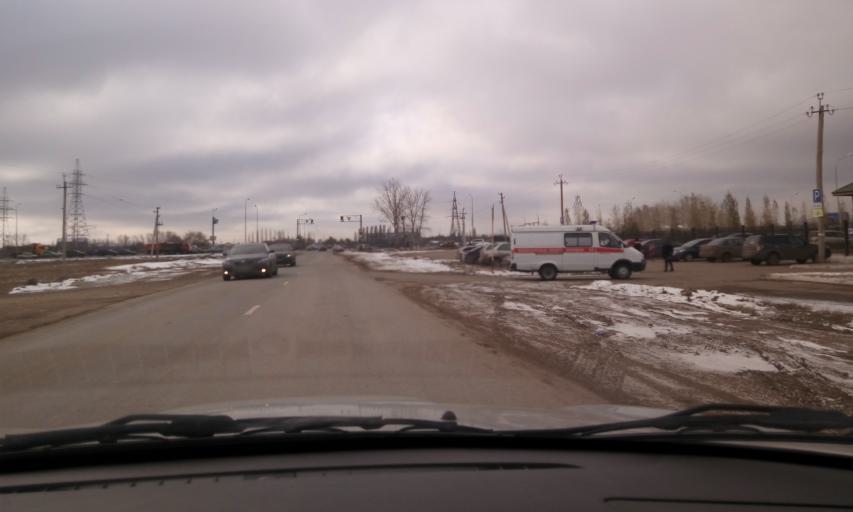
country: KZ
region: Astana Qalasy
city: Astana
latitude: 51.1397
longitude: 71.5298
